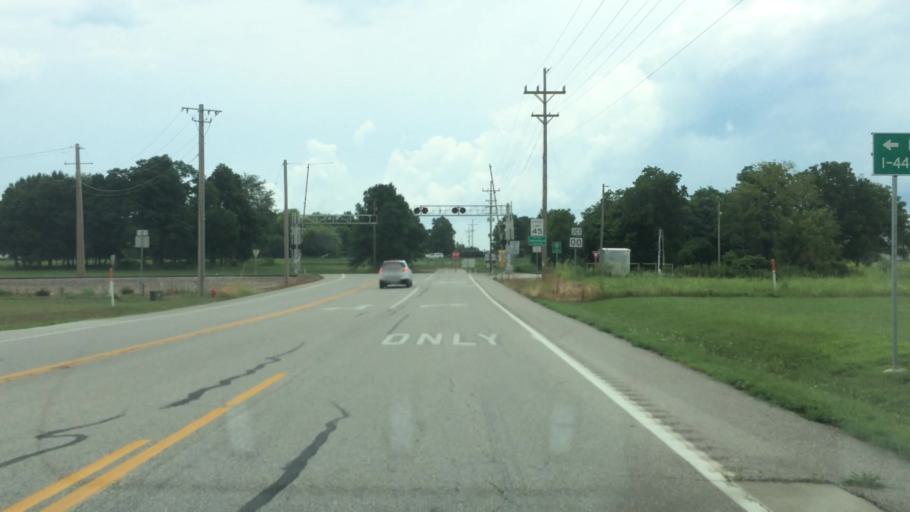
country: US
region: Missouri
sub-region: Greene County
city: Strafford
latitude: 37.2640
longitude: -93.1357
